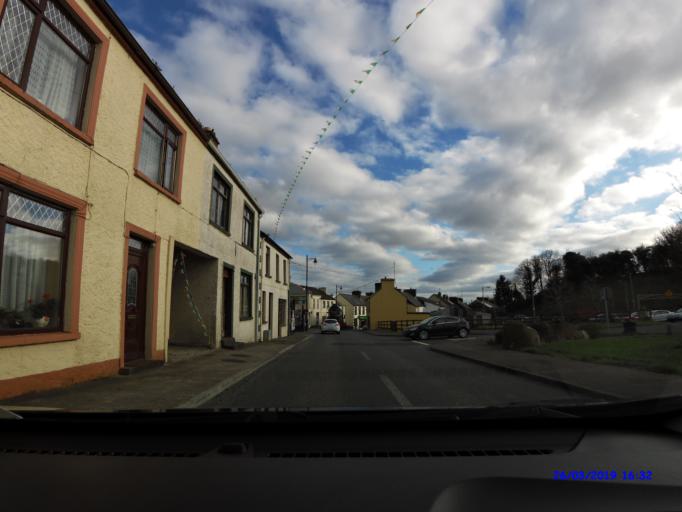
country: IE
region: Connaught
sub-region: Maigh Eo
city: Swinford
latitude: 53.8725
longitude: -8.8504
